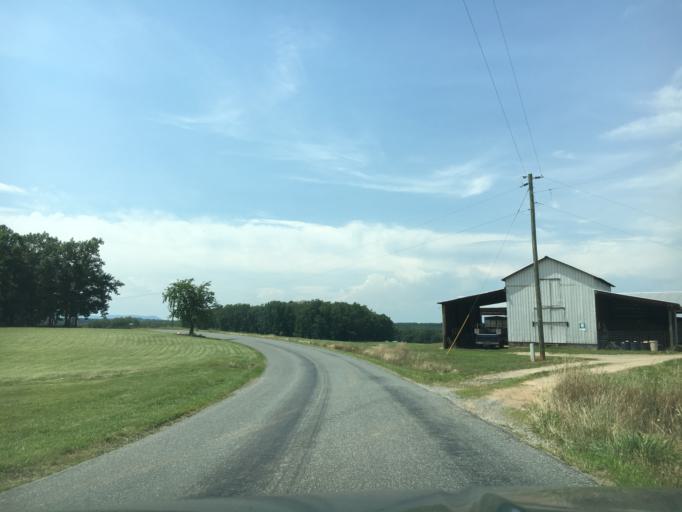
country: US
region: Virginia
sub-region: Pittsylvania County
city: Gretna
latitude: 36.9062
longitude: -79.4089
